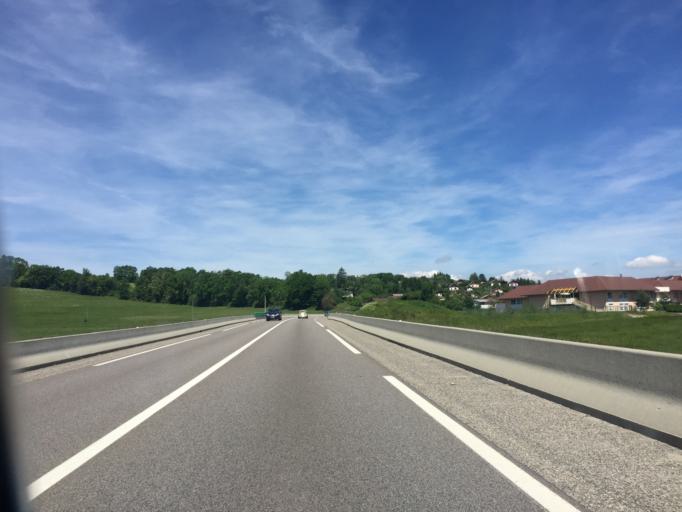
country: FR
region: Rhone-Alpes
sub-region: Departement de la Haute-Savoie
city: La Balme-de-Sillingy
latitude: 45.9559
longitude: 6.0368
